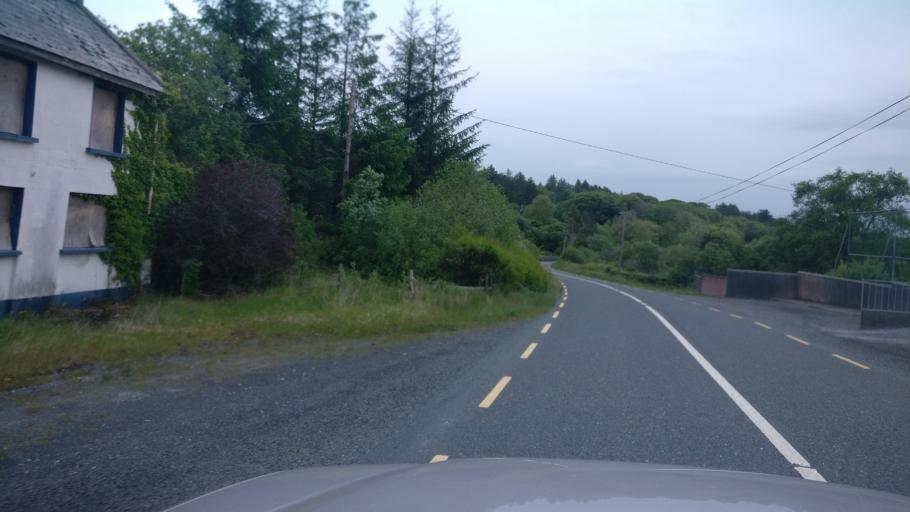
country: IE
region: Connaught
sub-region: County Galway
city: Loughrea
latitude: 53.0645
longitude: -8.6181
